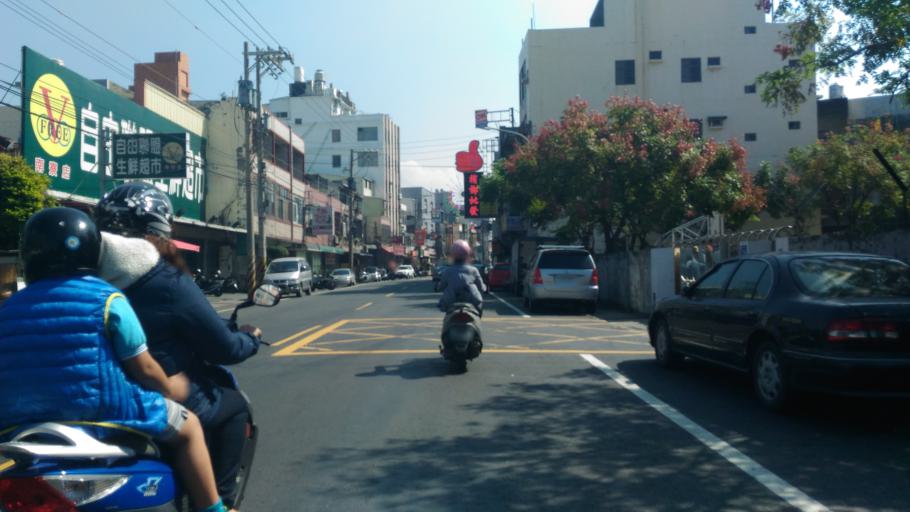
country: TW
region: Taiwan
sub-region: Hsinchu
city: Hsinchu
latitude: 24.8413
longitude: 120.9362
